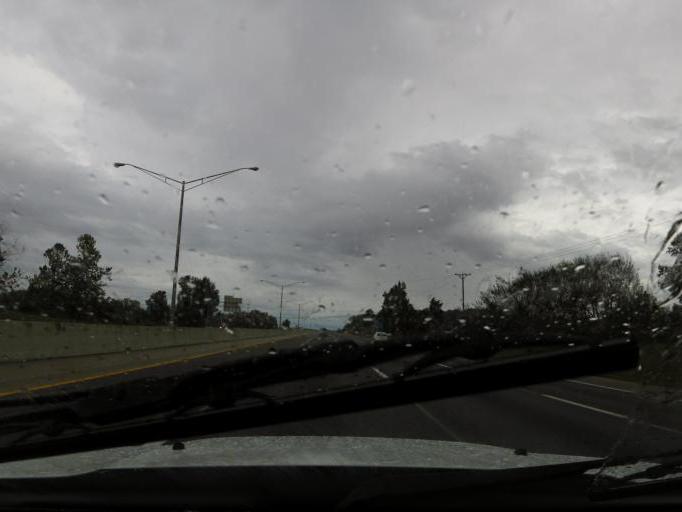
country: US
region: Kentucky
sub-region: Laurel County
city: London
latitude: 37.1278
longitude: -84.1074
